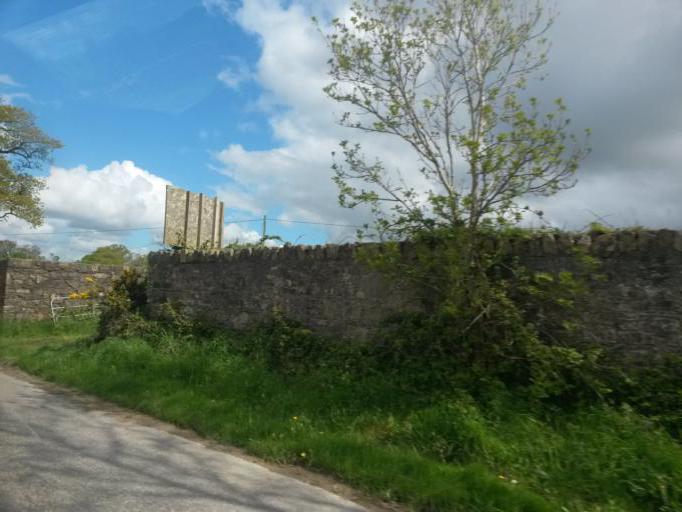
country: IE
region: Leinster
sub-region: Loch Garman
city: Enniscorthy
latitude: 52.4508
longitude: -6.5505
